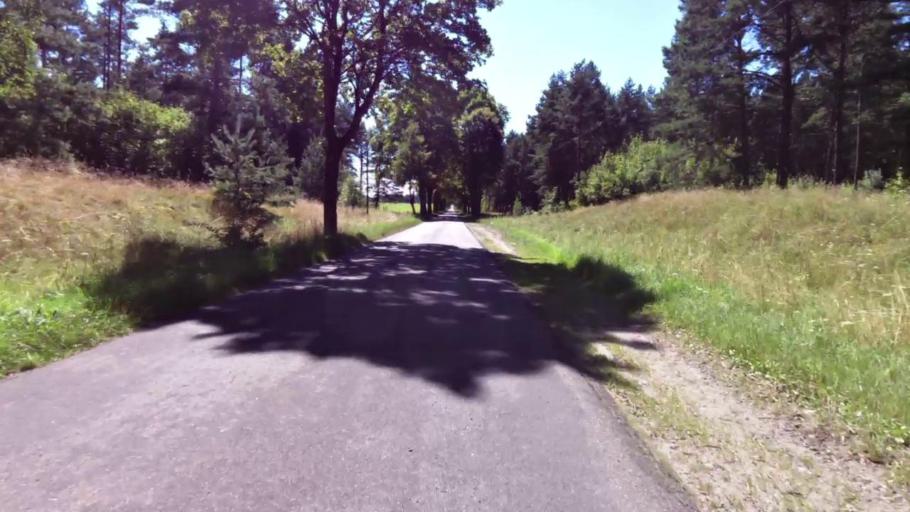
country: PL
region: West Pomeranian Voivodeship
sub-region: Powiat szczecinecki
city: Bialy Bor
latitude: 53.8832
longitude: 16.8086
